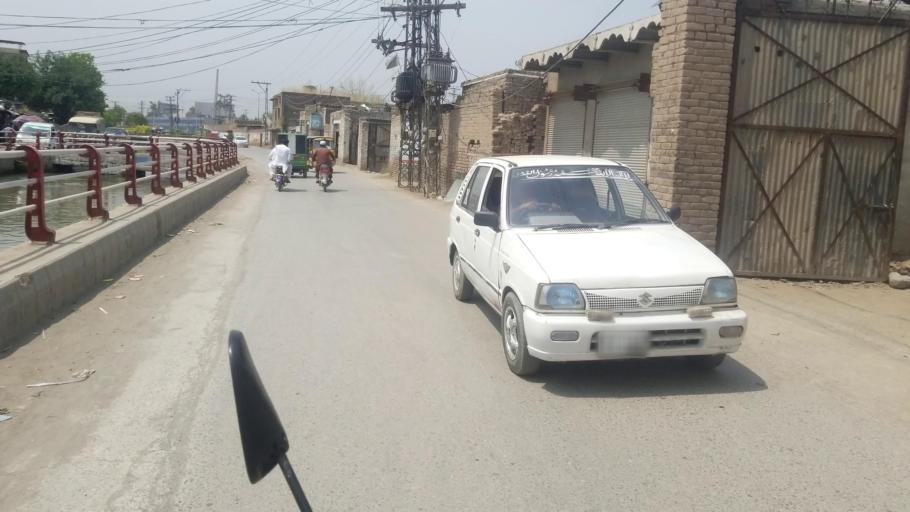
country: PK
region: Khyber Pakhtunkhwa
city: Peshawar
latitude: 34.0154
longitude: 71.6068
